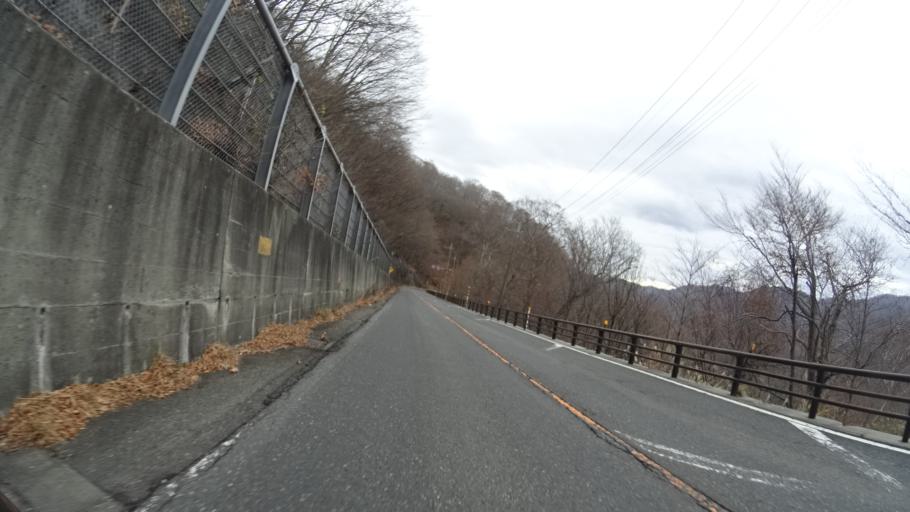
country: JP
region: Gunma
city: Nakanojomachi
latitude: 36.7494
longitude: 138.8330
